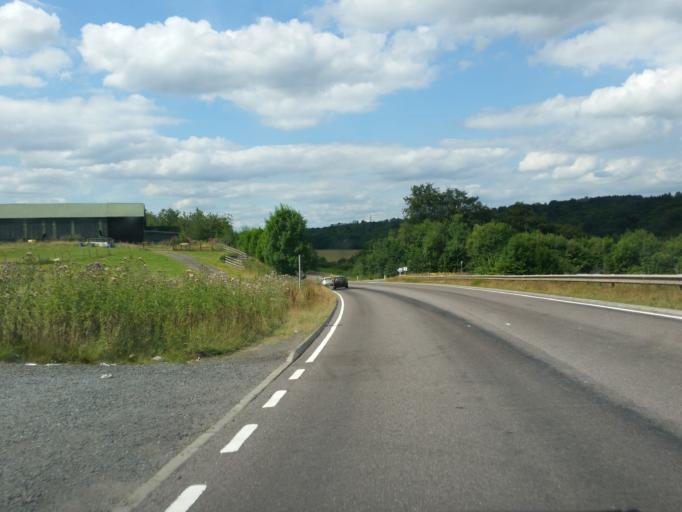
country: GB
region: Scotland
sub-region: North Lanarkshire
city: Overtown
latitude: 55.7423
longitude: -3.9299
